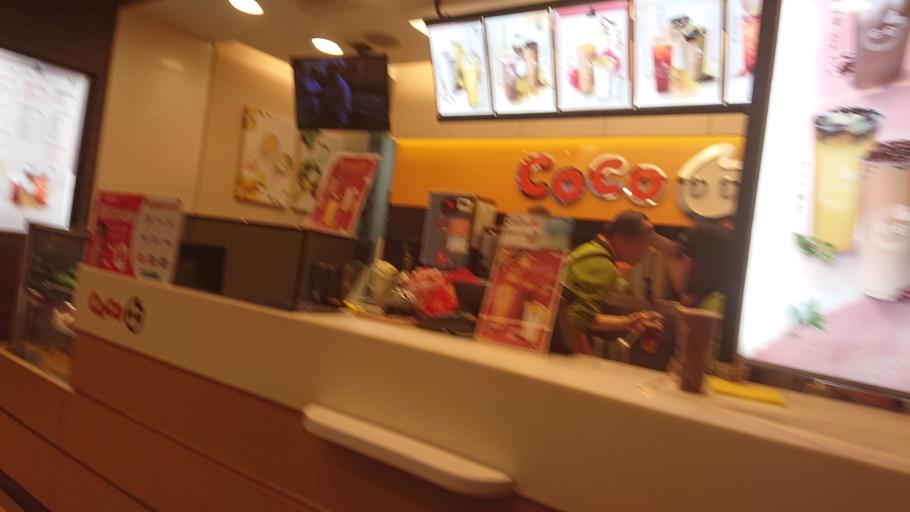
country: TW
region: Taipei
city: Taipei
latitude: 25.1834
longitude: 121.4242
